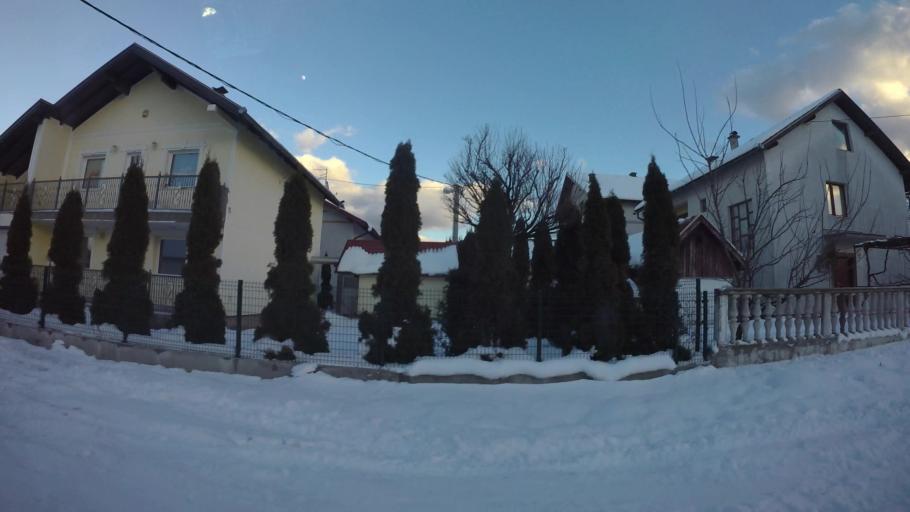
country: BA
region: Federation of Bosnia and Herzegovina
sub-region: Kanton Sarajevo
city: Sarajevo
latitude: 43.8078
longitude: 18.3670
